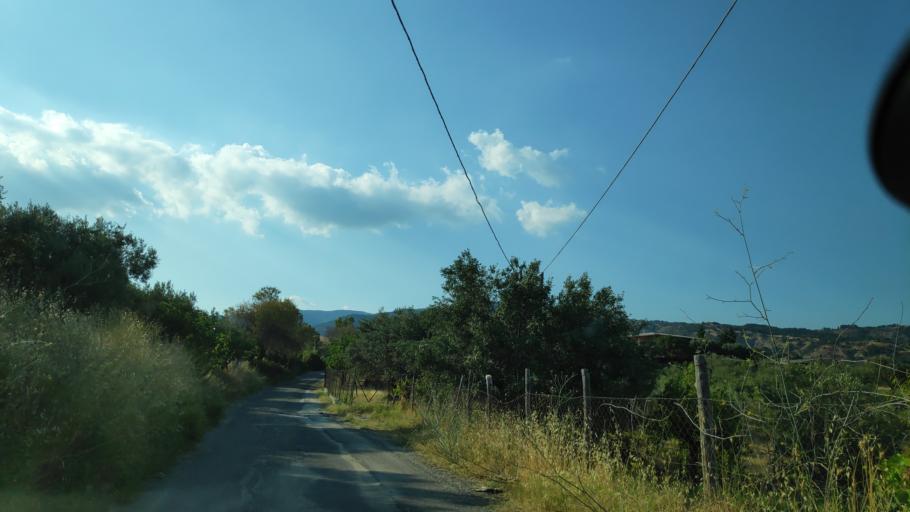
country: IT
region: Calabria
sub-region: Provincia di Catanzaro
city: Guardavalle
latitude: 38.5099
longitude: 16.5043
